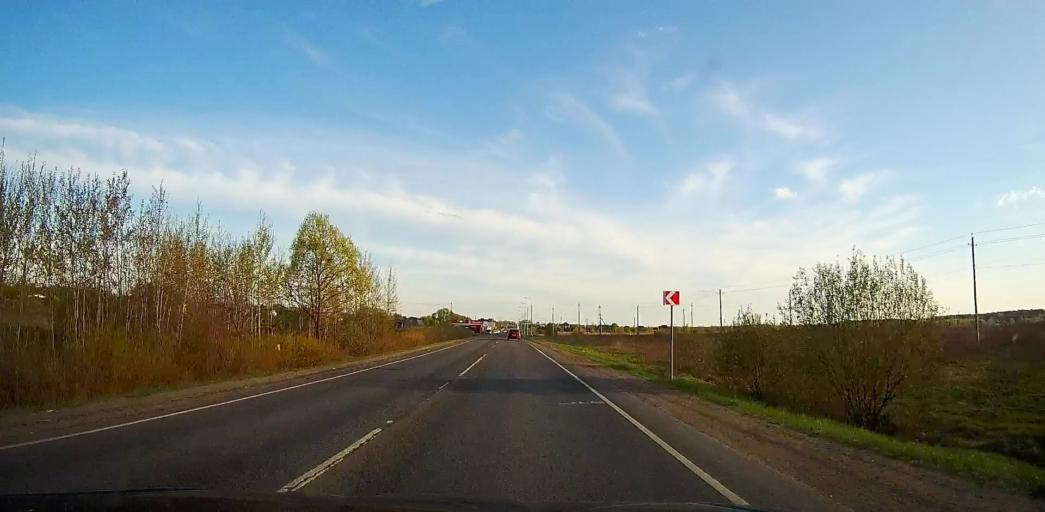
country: RU
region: Moskovskaya
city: Bronnitsy
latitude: 55.3330
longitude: 38.2195
